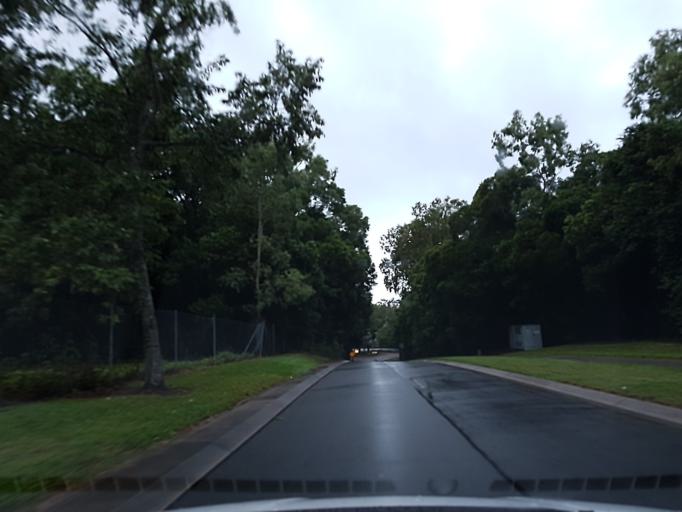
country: AU
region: Queensland
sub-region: Cairns
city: Palm Cove
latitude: -16.7520
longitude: 145.6686
